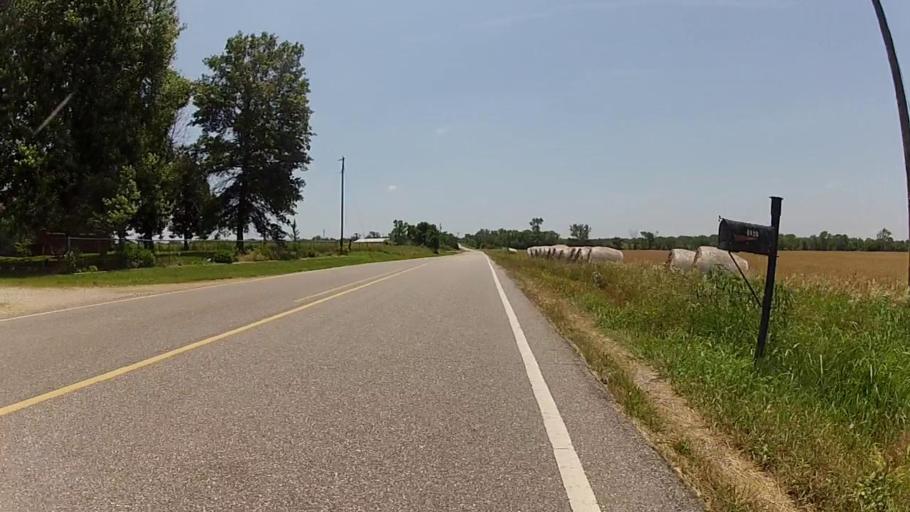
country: US
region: Kansas
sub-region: Montgomery County
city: Cherryvale
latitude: 37.1967
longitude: -95.5394
